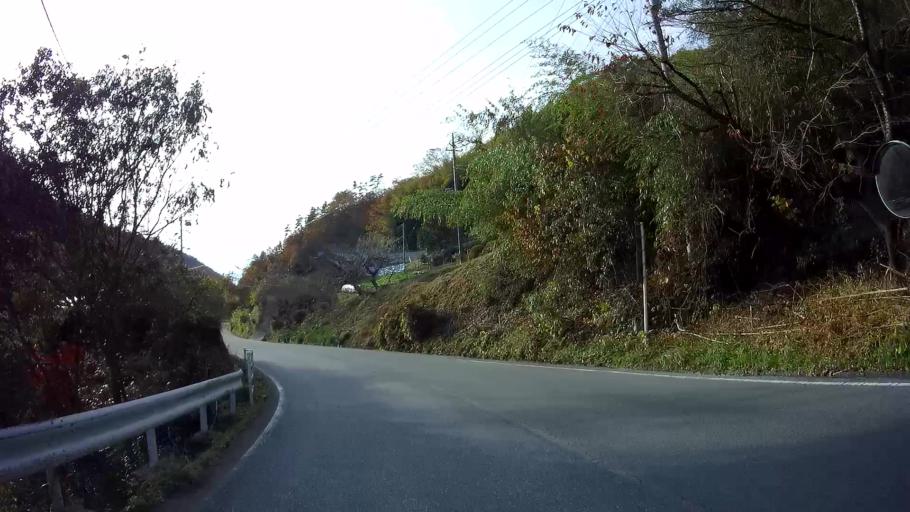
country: JP
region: Yamanashi
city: Fujikawaguchiko
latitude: 35.4755
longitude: 138.5528
